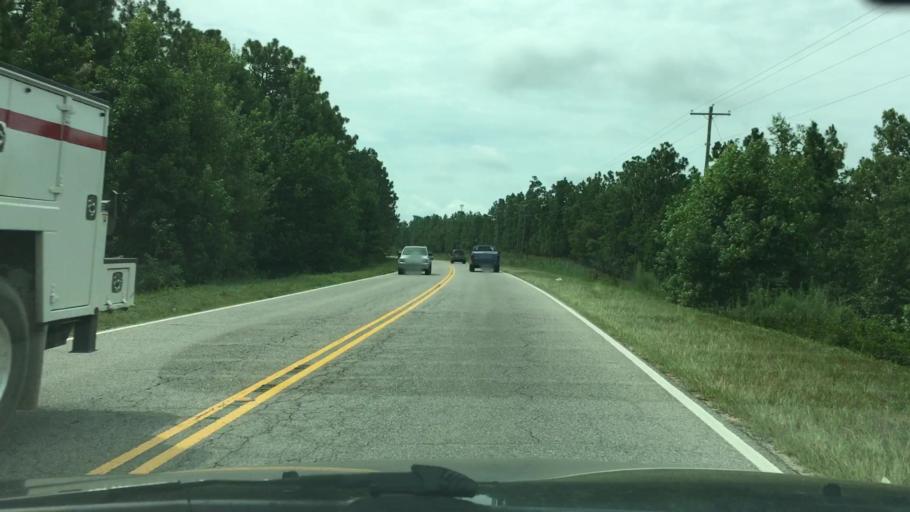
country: US
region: South Carolina
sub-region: Aiken County
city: Warrenville
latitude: 33.5363
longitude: -81.7742
